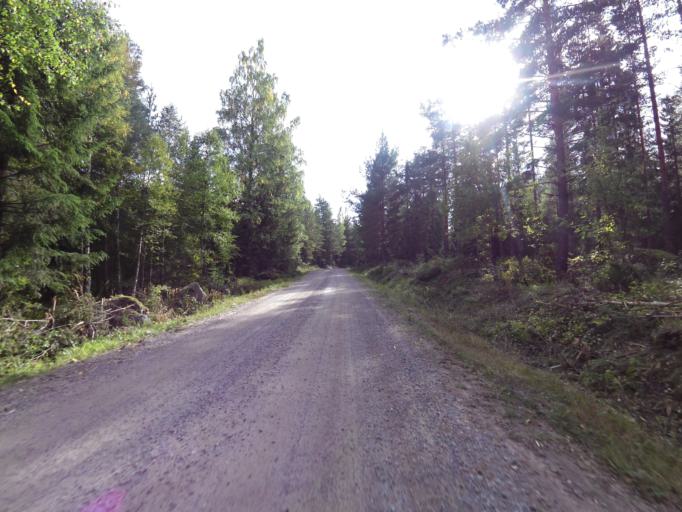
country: SE
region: Gaevleborg
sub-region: Sandvikens Kommun
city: Sandviken
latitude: 60.7424
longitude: 16.8353
